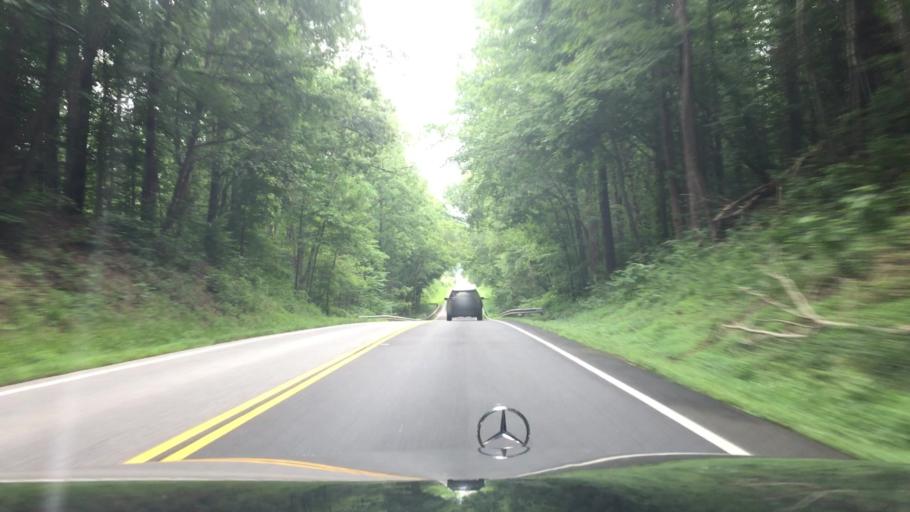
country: US
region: Virginia
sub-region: Nottoway County
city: Crewe
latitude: 37.2734
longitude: -78.1474
